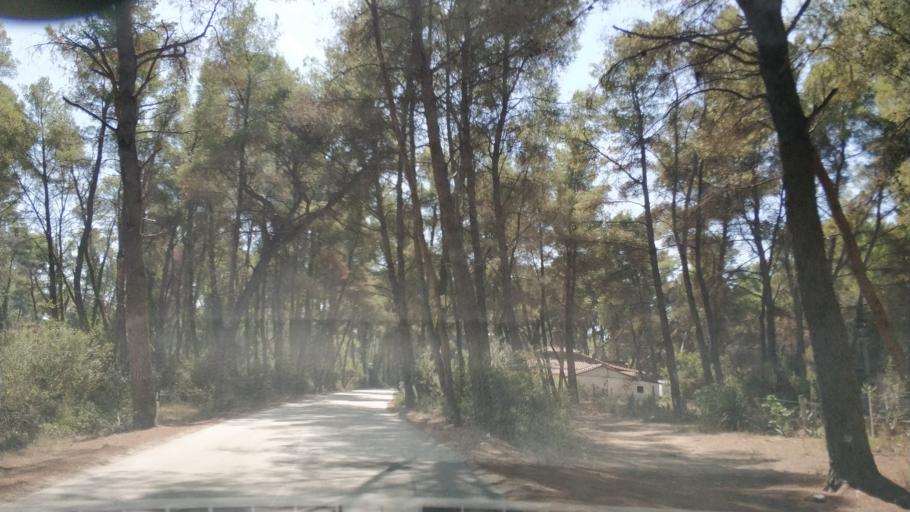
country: AL
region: Fier
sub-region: Rrethi i Lushnjes
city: Divjake
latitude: 40.9763
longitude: 19.4810
